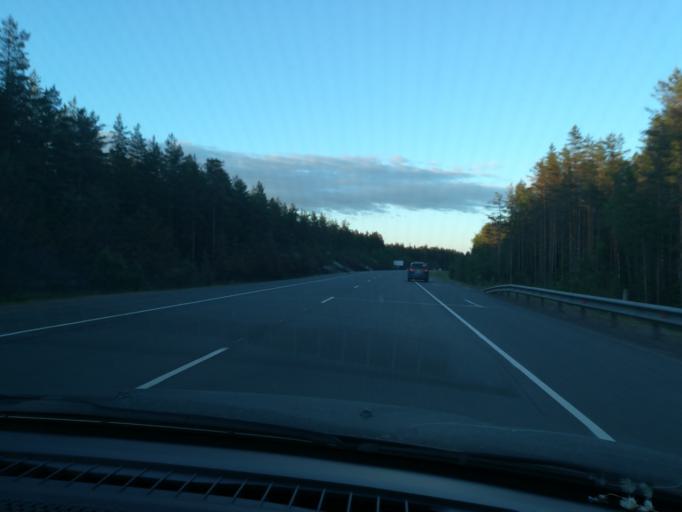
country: RU
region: Leningrad
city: Roshchino
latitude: 60.3603
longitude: 29.5996
